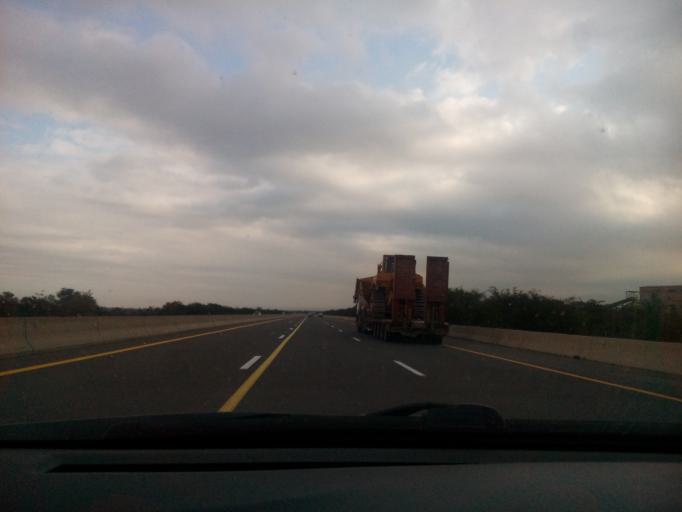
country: DZ
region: Relizane
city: Relizane
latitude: 35.7895
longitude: 0.4210
